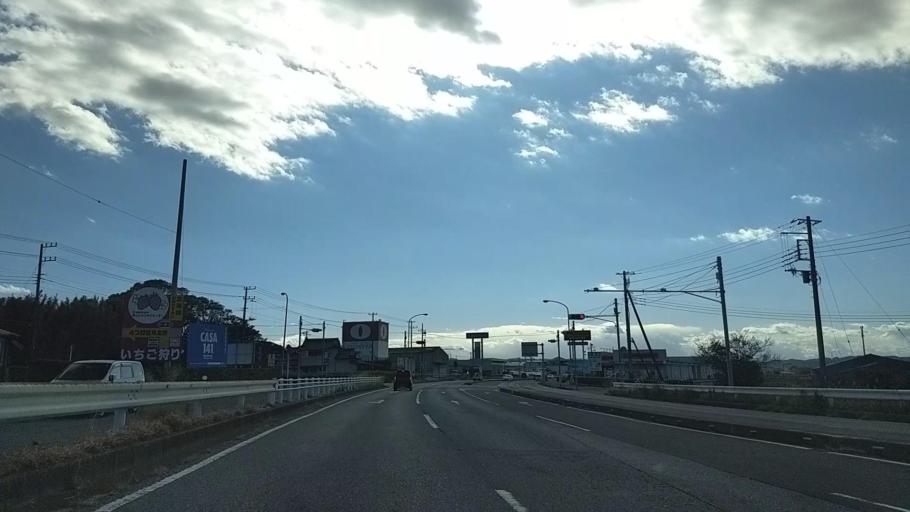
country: JP
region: Chiba
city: Tateyama
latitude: 35.0193
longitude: 139.8709
